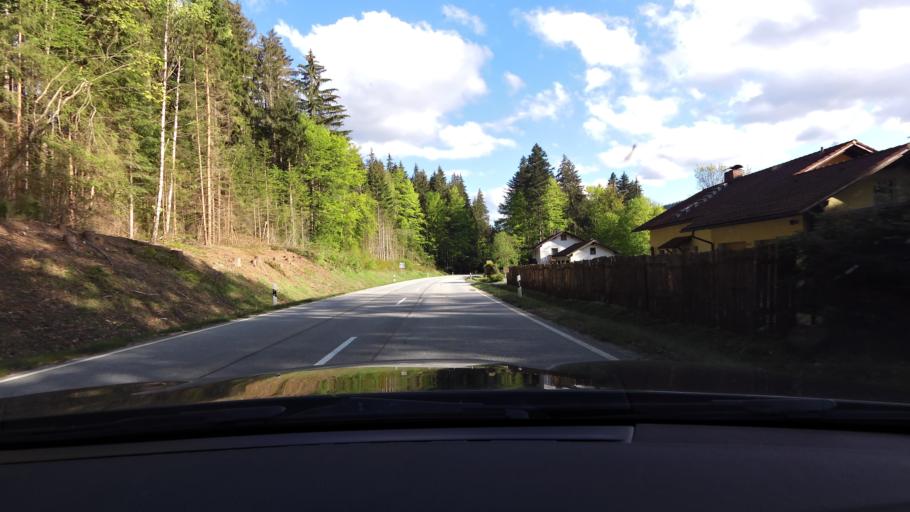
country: DE
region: Bavaria
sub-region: Lower Bavaria
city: Bayerisch Eisenstein
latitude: 49.0802
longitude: 13.2087
